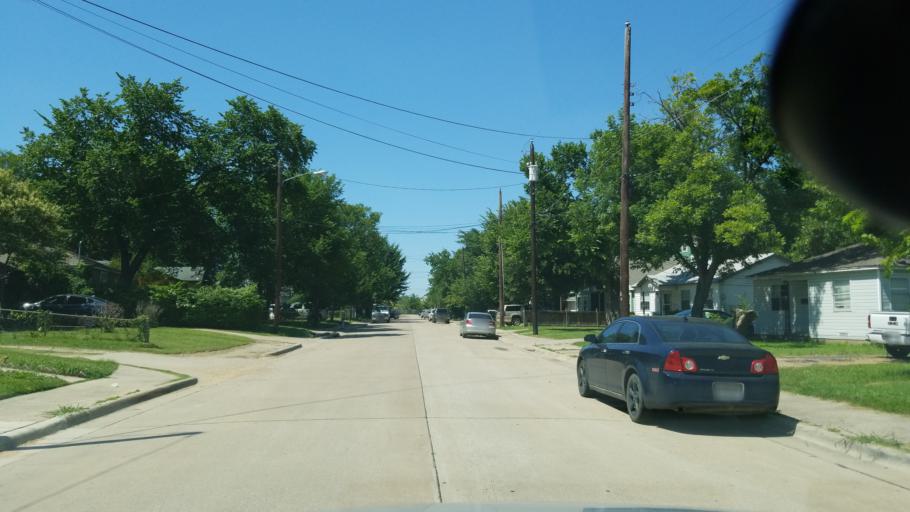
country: US
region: Texas
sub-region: Dallas County
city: Irving
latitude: 32.8310
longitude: -96.9400
